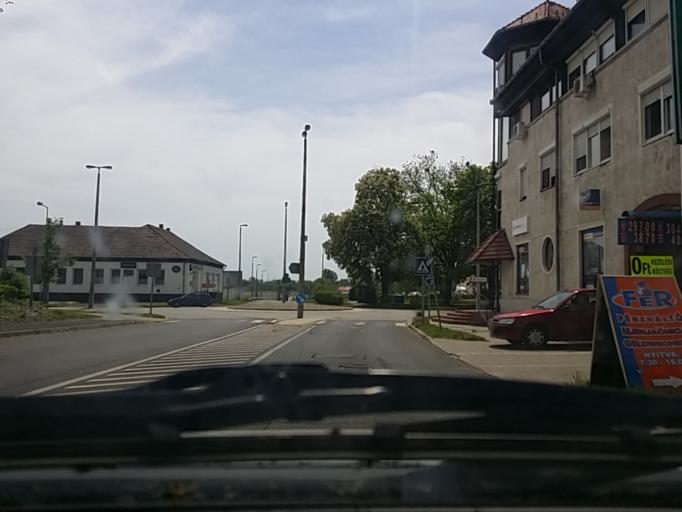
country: HU
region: Somogy
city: Barcs
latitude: 45.9597
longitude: 17.4667
